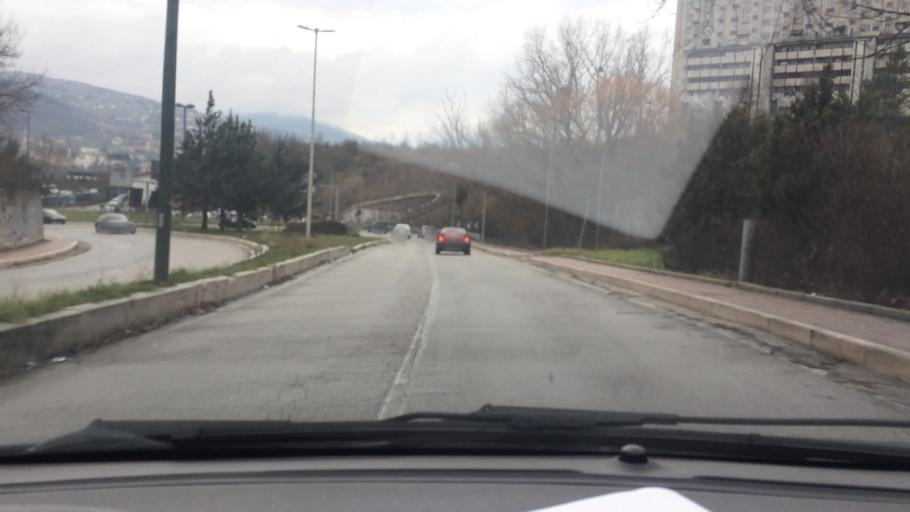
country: IT
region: Basilicate
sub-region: Provincia di Potenza
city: Potenza
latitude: 40.6330
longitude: 15.7940
